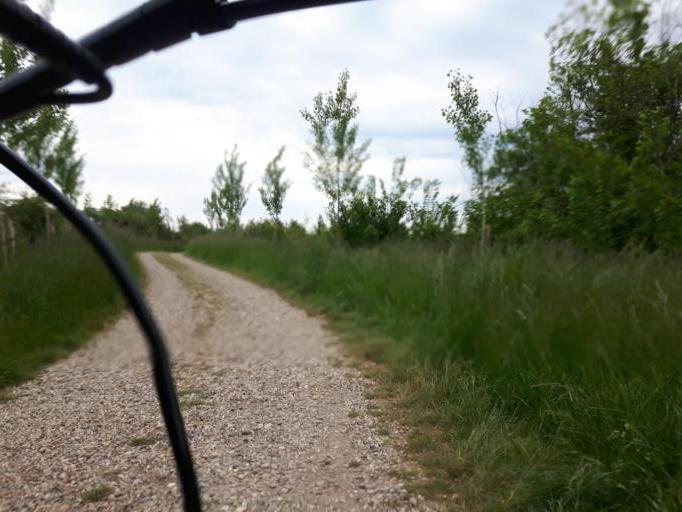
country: NL
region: Zeeland
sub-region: Gemeente Goes
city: Goes
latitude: 51.4476
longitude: 3.8322
